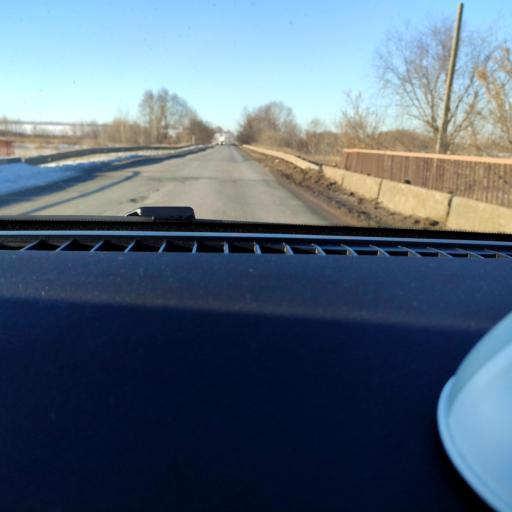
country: RU
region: Samara
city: Spiridonovka
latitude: 53.1444
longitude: 50.5555
